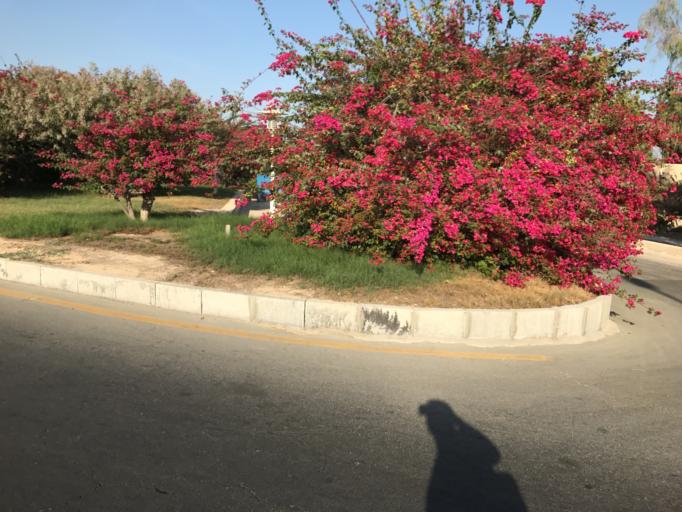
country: IR
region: Hormozgan
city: Kish
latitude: 26.5414
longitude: 54.0227
